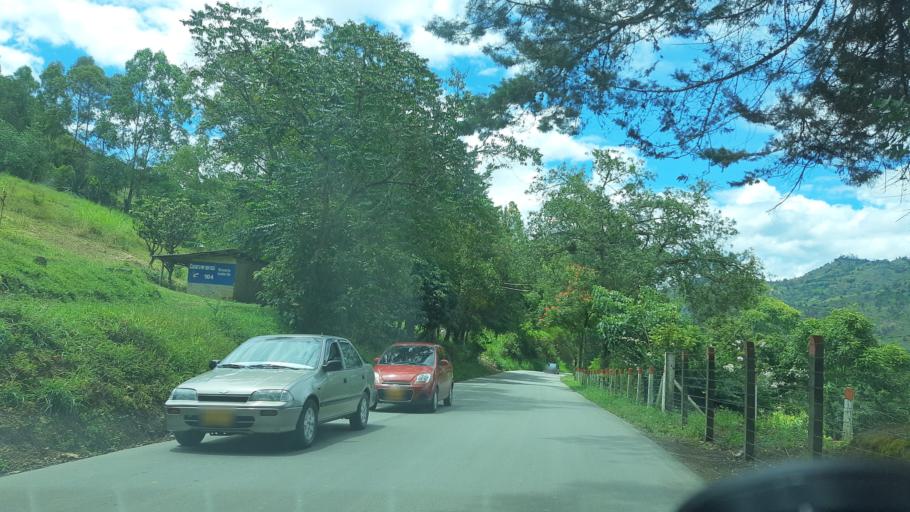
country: CO
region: Boyaca
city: Garagoa
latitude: 5.0535
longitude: -73.3855
